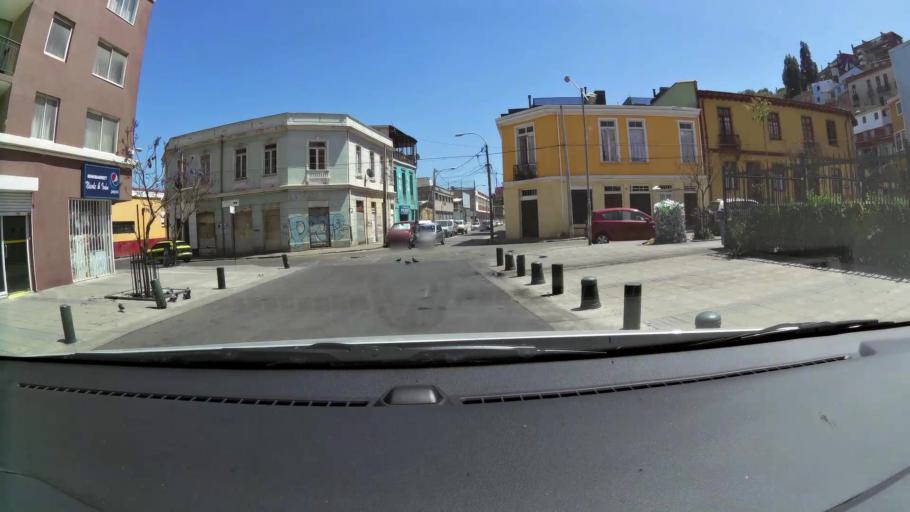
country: CL
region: Valparaiso
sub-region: Provincia de Valparaiso
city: Valparaiso
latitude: -33.0482
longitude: -71.6027
